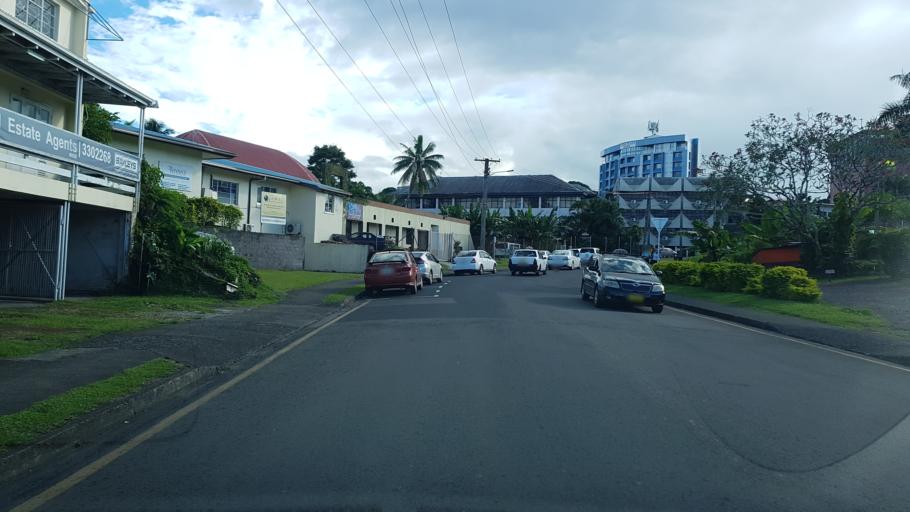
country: FJ
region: Central
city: Suva
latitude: -18.1447
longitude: 178.4246
